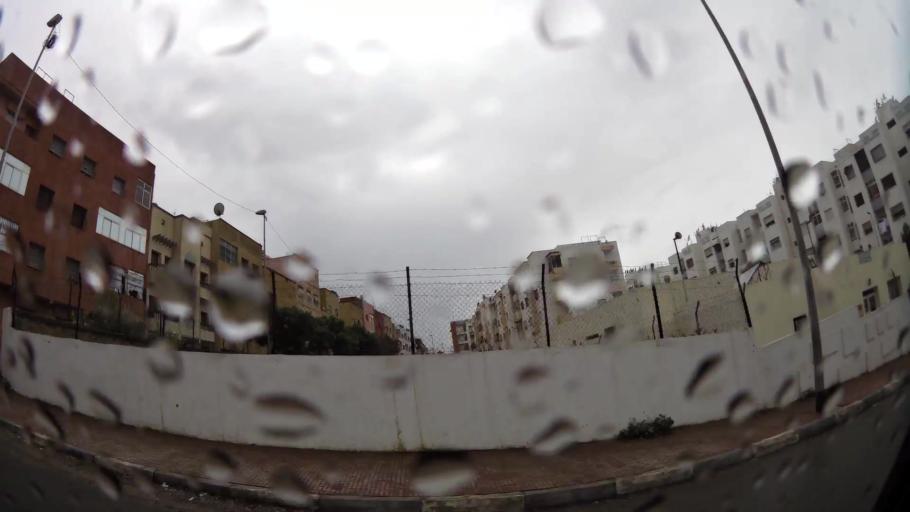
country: MA
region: Grand Casablanca
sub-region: Mediouna
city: Tit Mellil
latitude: 33.6232
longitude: -7.4840
